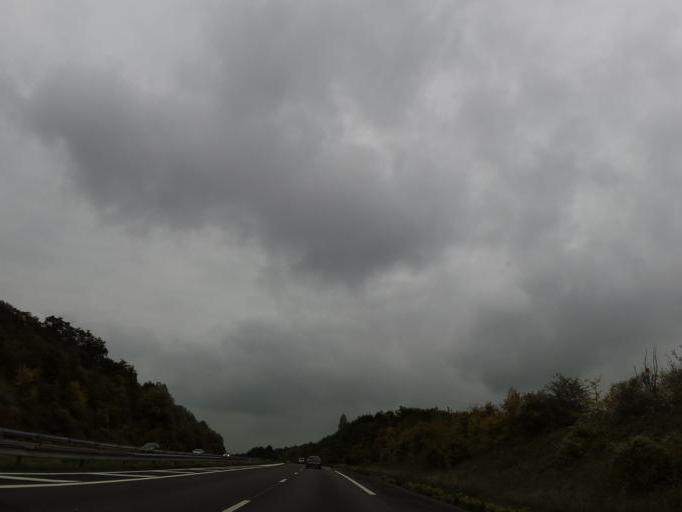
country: FR
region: Lorraine
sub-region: Departement de la Moselle
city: Longeville-les-Saint-Avold
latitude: 49.1327
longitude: 6.5731
